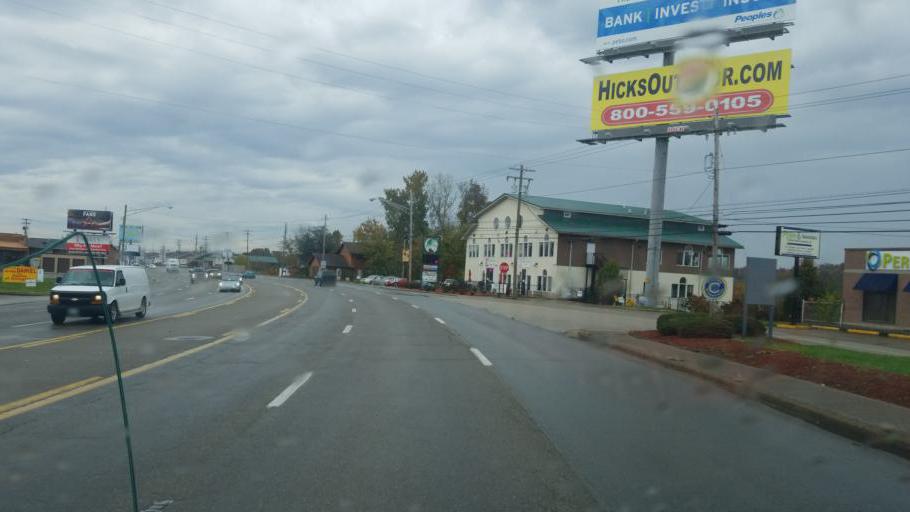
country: US
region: West Virginia
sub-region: Wood County
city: Vienna
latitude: 39.3198
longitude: -81.5536
